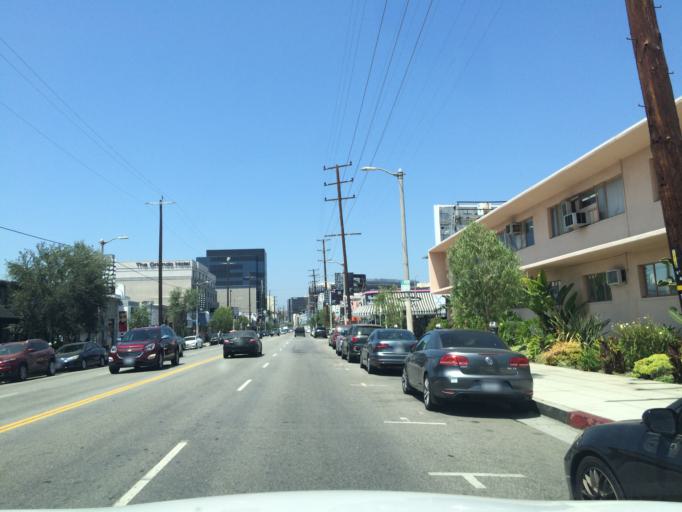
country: US
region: California
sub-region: Los Angeles County
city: West Hollywood
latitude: 34.0728
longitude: -118.3713
